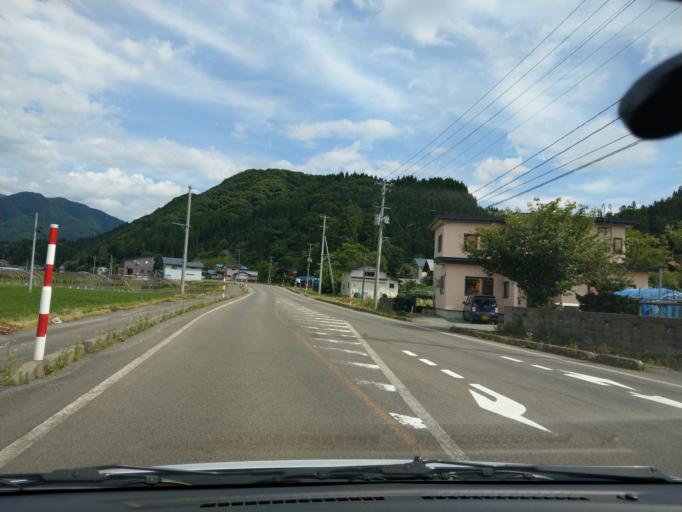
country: JP
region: Akita
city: Kakunodatemachi
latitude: 39.6760
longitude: 140.5654
